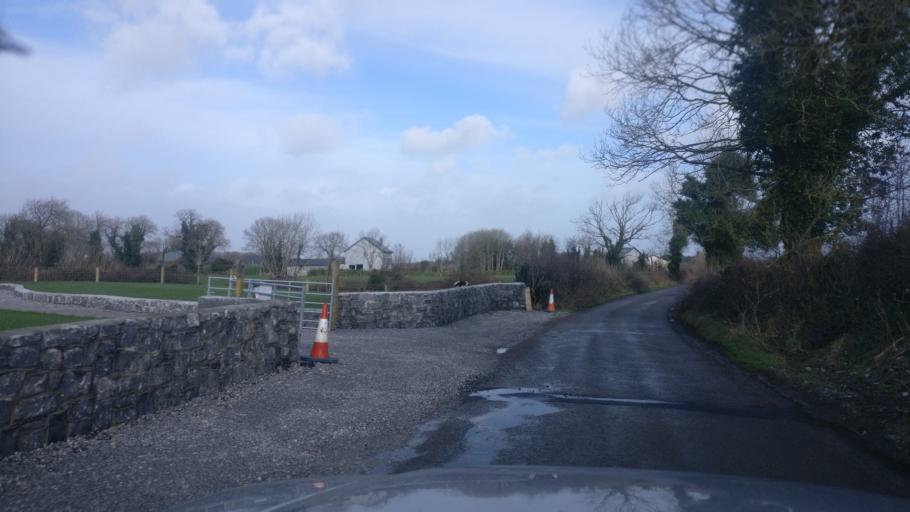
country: IE
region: Connaught
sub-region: County Galway
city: Loughrea
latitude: 53.2627
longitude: -8.5808
